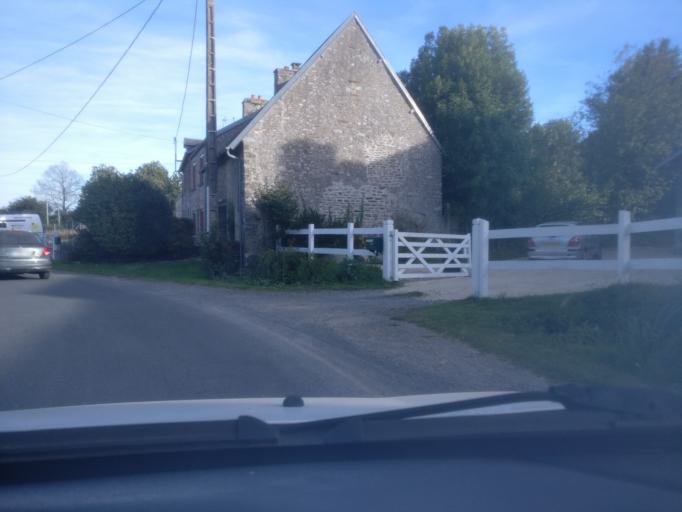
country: FR
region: Lower Normandy
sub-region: Departement de la Manche
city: Sartilly
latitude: 48.7115
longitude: -1.4897
